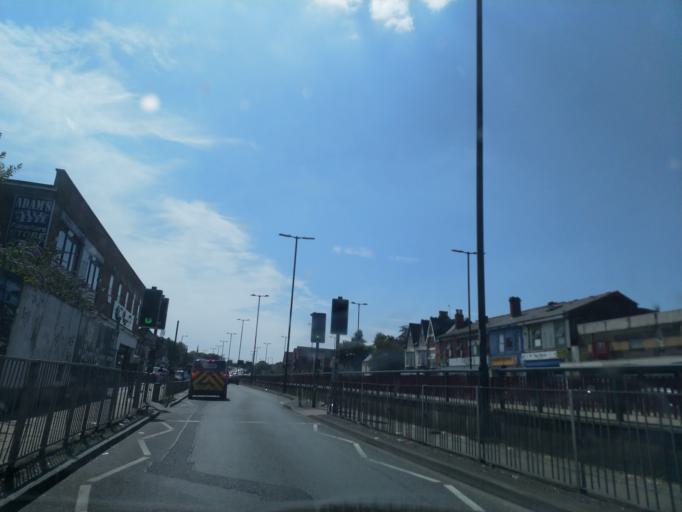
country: GB
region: England
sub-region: City and Borough of Birmingham
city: Hockley
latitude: 52.5149
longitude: -1.9016
